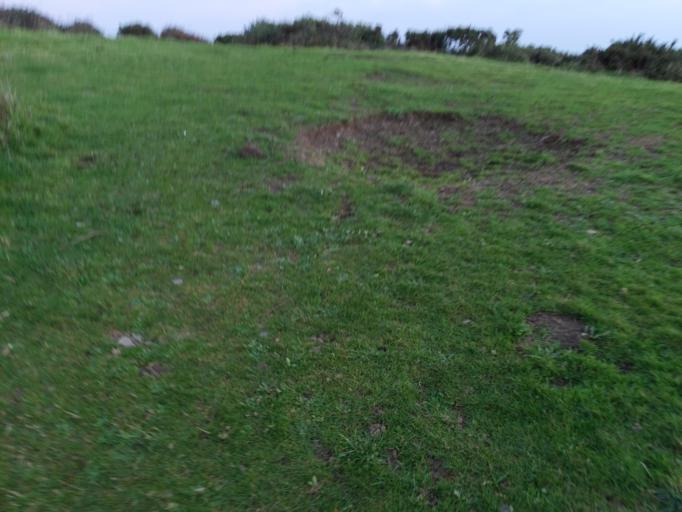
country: GB
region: England
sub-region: Cornwall
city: Fowey
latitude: 50.3253
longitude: -4.6002
